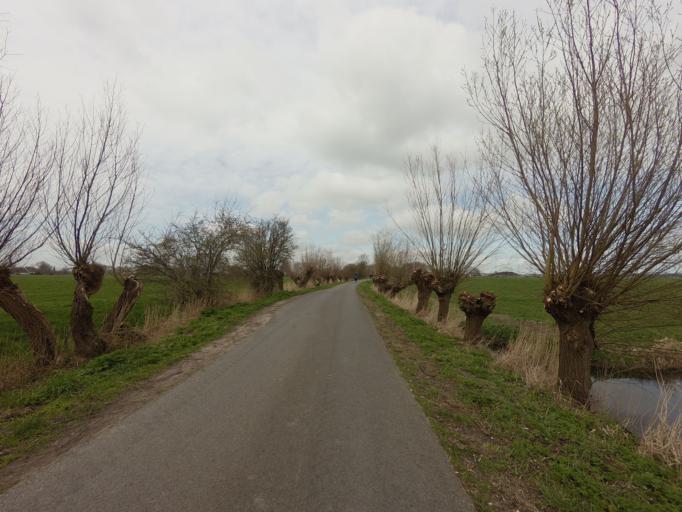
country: NL
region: North Holland
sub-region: Gemeente Amsterdam
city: Driemond
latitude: 52.2766
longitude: 5.0067
